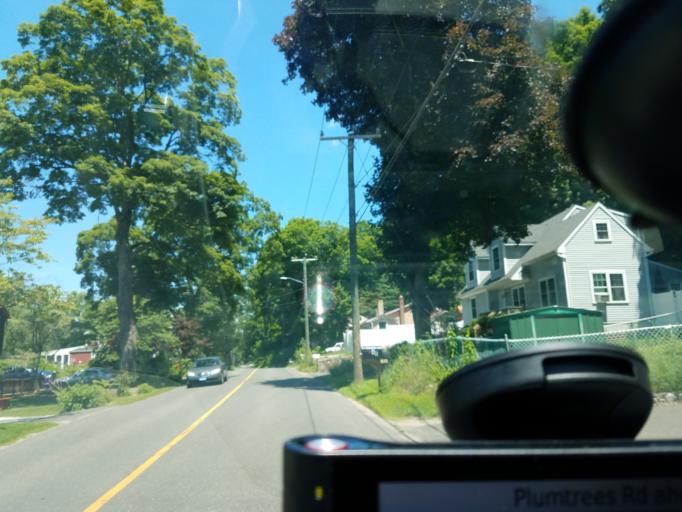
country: US
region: Connecticut
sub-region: Fairfield County
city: Bethel
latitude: 41.3816
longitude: -73.3990
